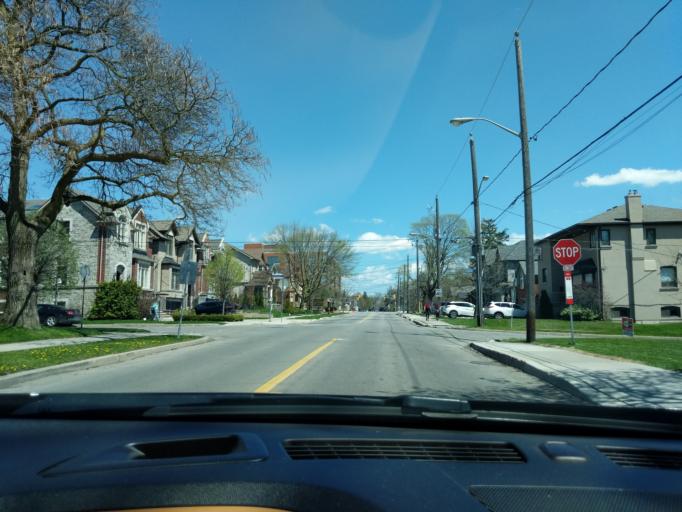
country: CA
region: Ontario
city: Toronto
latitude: 43.7118
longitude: -79.4307
